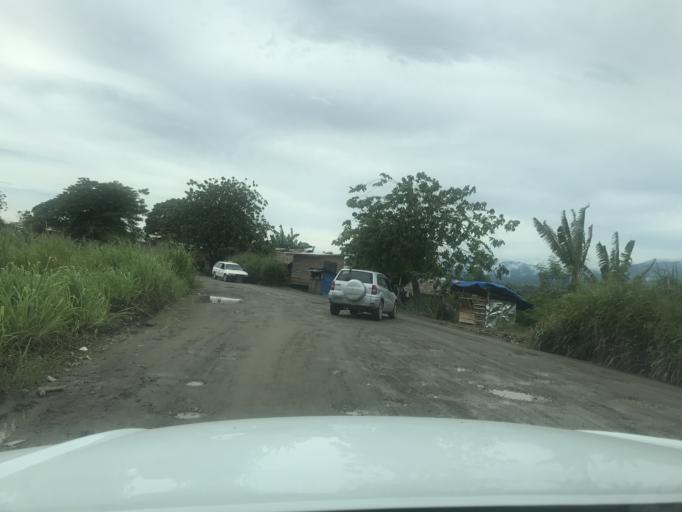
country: SB
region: Guadalcanal
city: Honiara
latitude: -9.4358
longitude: 160.0367
